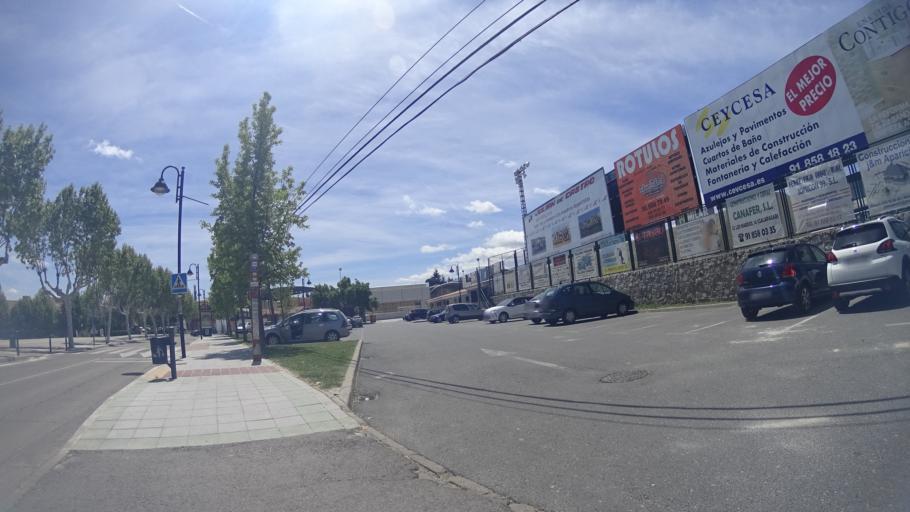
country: ES
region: Madrid
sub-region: Provincia de Madrid
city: Galapagar
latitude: 40.5825
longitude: -4.0092
